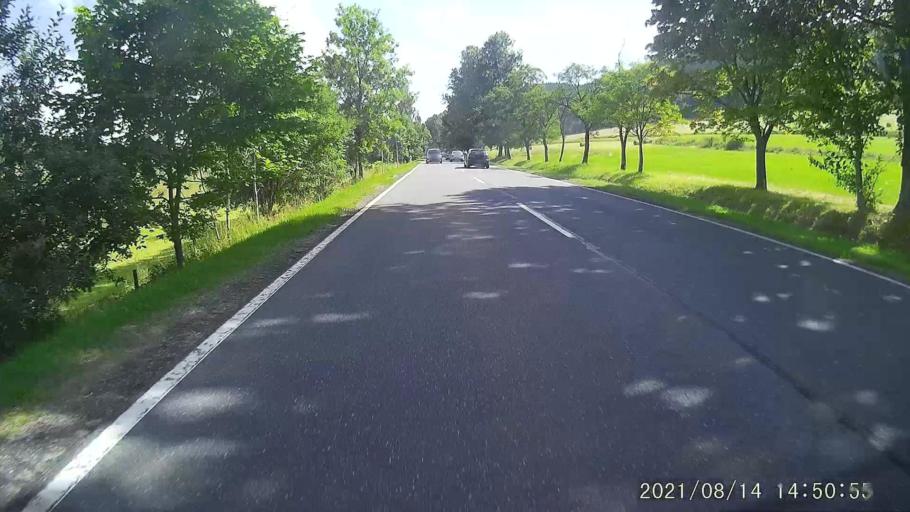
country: PL
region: Lower Silesian Voivodeship
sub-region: Powiat walbrzyski
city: Gluszyca Gorna
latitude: 50.6570
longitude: 16.3738
